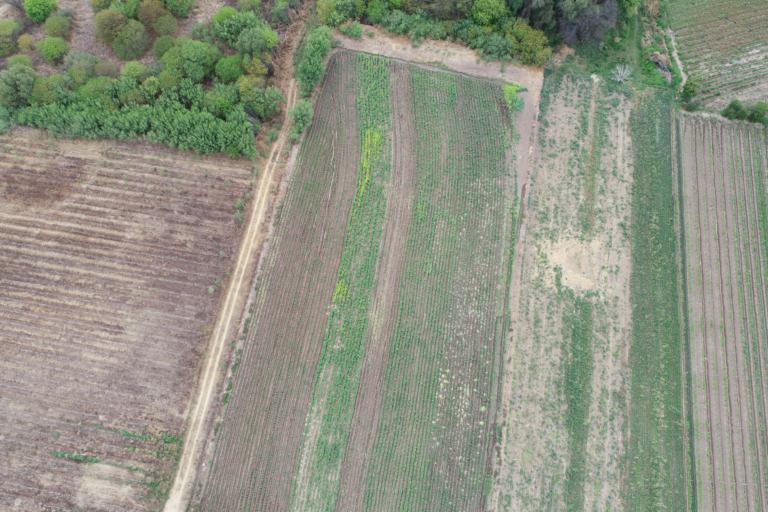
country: BO
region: Tarija
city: Tarija
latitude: -21.5983
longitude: -64.6156
